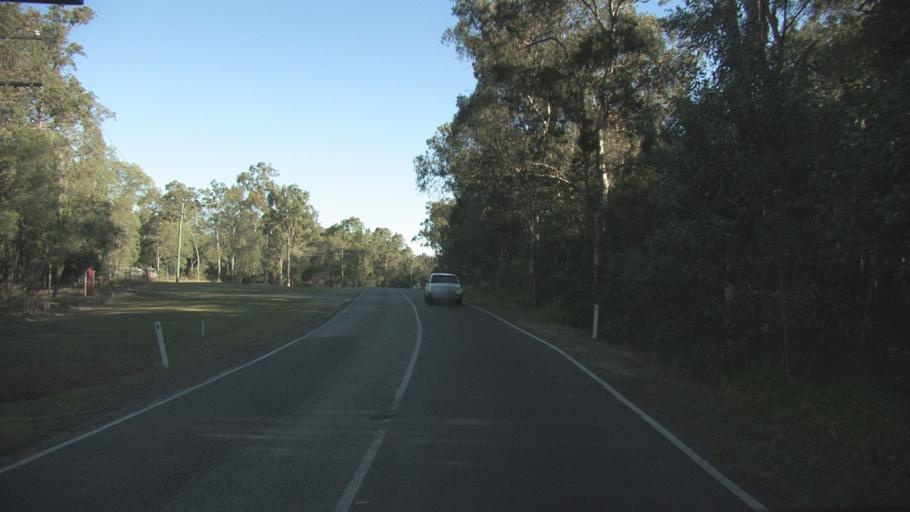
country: AU
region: Queensland
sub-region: Logan
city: Chambers Flat
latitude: -27.7551
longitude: 153.0498
